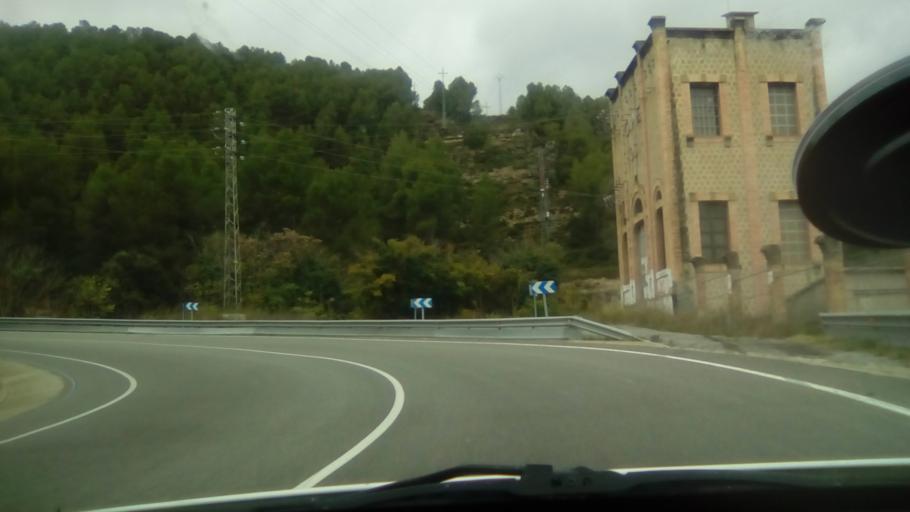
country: ES
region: Catalonia
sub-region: Provincia de Barcelona
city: Sant Fruitos de Bages
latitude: 41.7113
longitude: 1.8682
